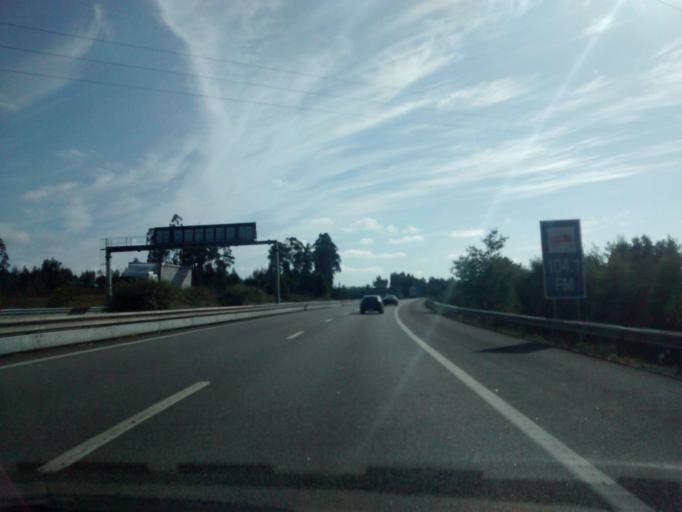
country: PT
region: Porto
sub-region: Santo Tirso
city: Santo Tirso
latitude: 41.3581
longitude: -8.5022
